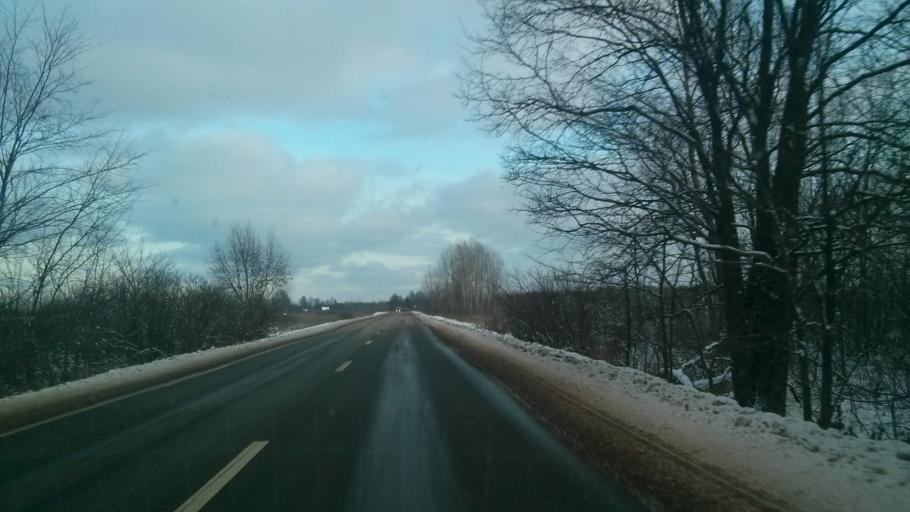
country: RU
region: Nizjnij Novgorod
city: Navashino
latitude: 55.6044
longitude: 42.1827
